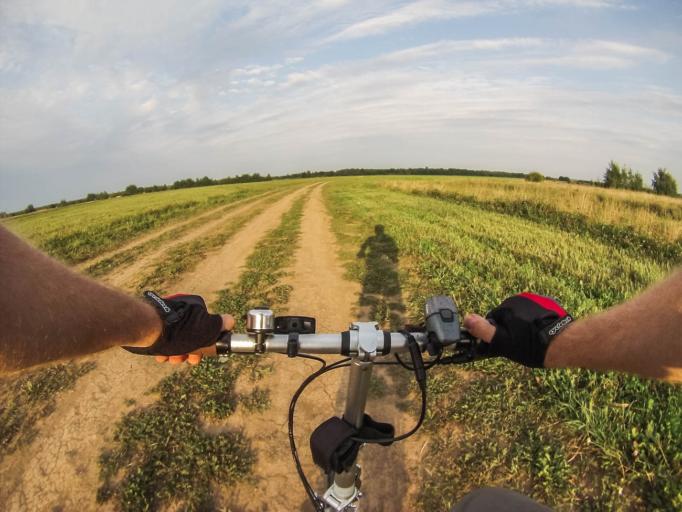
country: RU
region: Kostroma
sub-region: Kostromskoy Rayon
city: Kostroma
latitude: 57.8350
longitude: 40.8486
